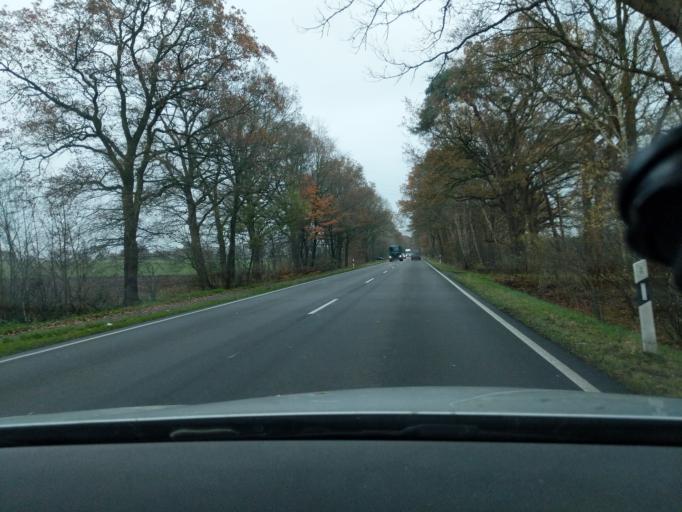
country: DE
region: Lower Saxony
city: Gyhum
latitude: 53.2244
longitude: 9.2919
